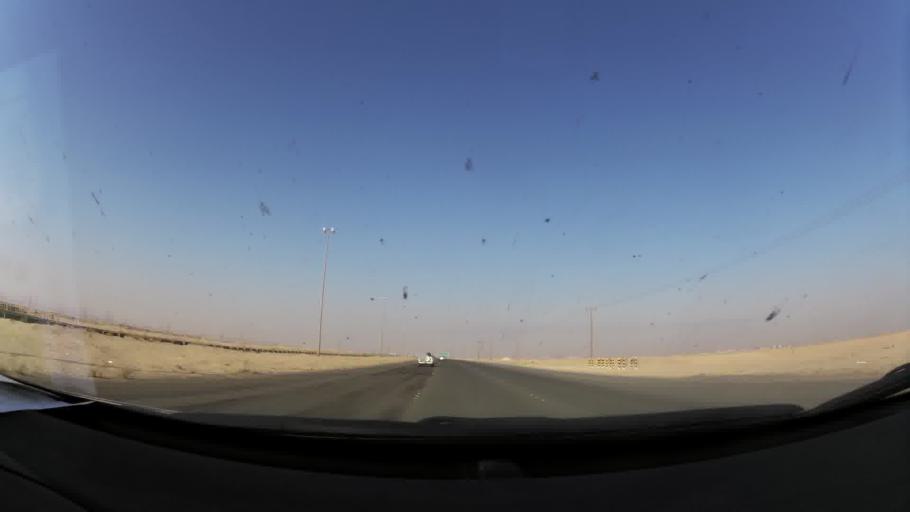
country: IQ
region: Basra Governorate
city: Umm Qasr
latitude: 29.8078
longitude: 47.6719
